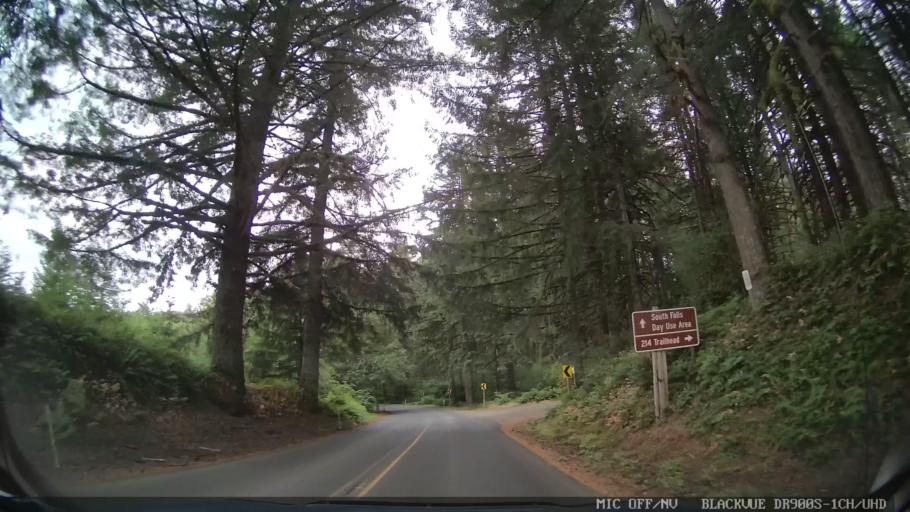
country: US
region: Oregon
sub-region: Linn County
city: Lyons
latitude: 44.8533
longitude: -122.6605
